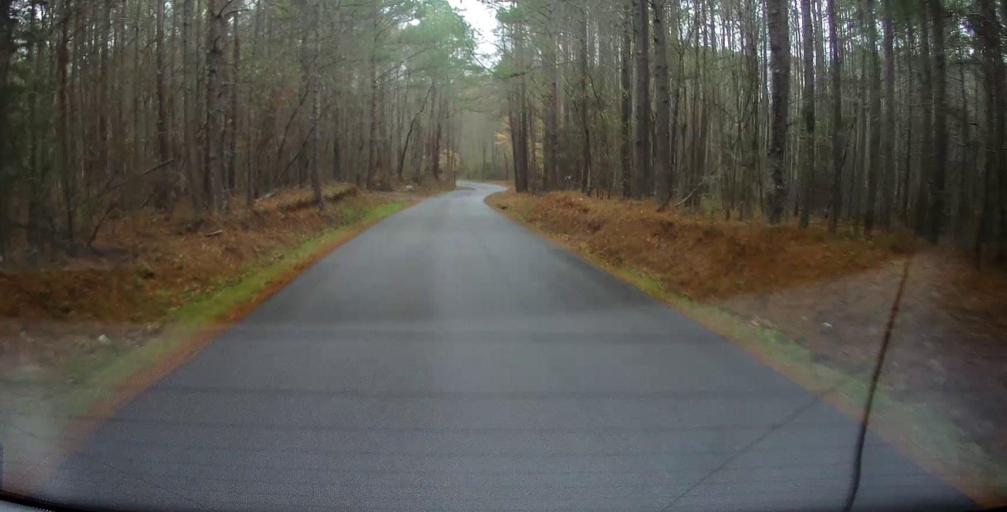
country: US
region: Georgia
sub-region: Monroe County
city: Forsyth
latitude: 33.0496
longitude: -83.8839
